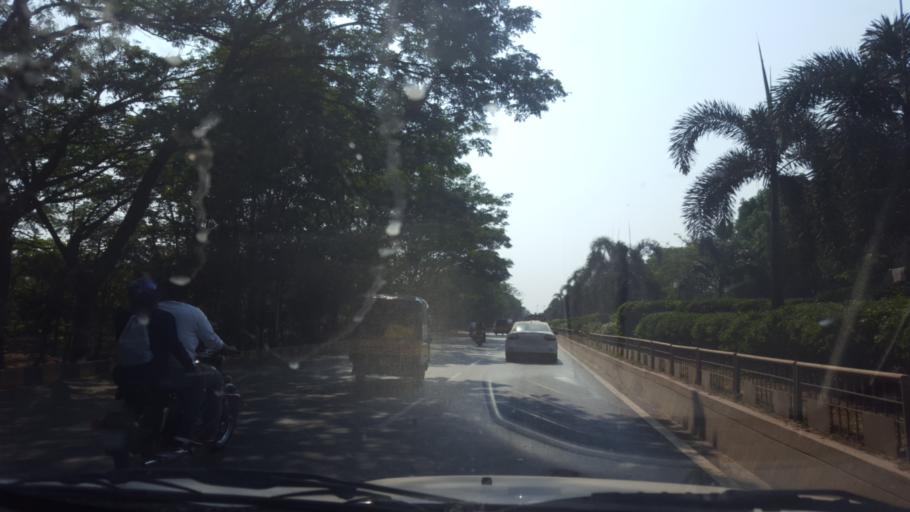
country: IN
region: Andhra Pradesh
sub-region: Vishakhapatnam
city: Gajuwaka
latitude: 17.7346
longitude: 83.2284
